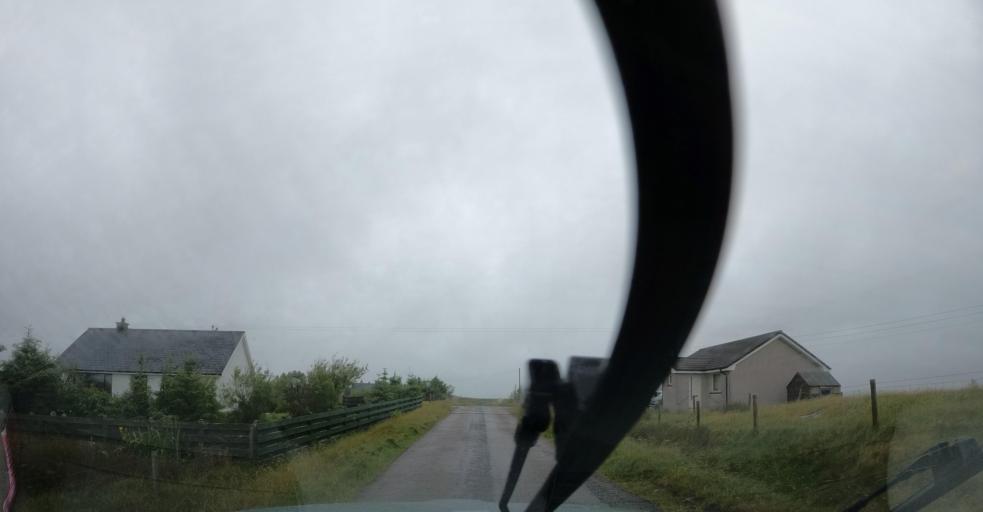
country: GB
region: Scotland
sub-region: Eilean Siar
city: Benbecula
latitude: 57.4994
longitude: -7.2542
